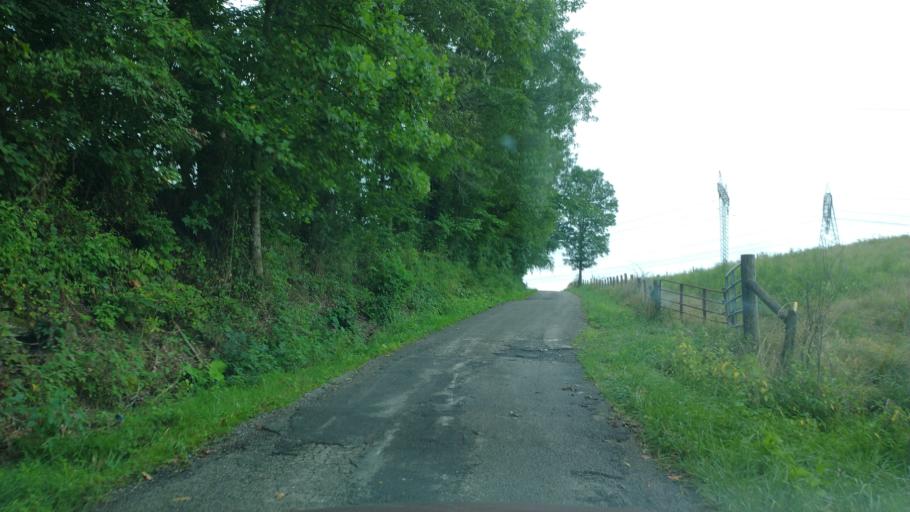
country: US
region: West Virginia
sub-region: Mason County
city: New Haven
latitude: 38.9243
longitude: -81.9478
